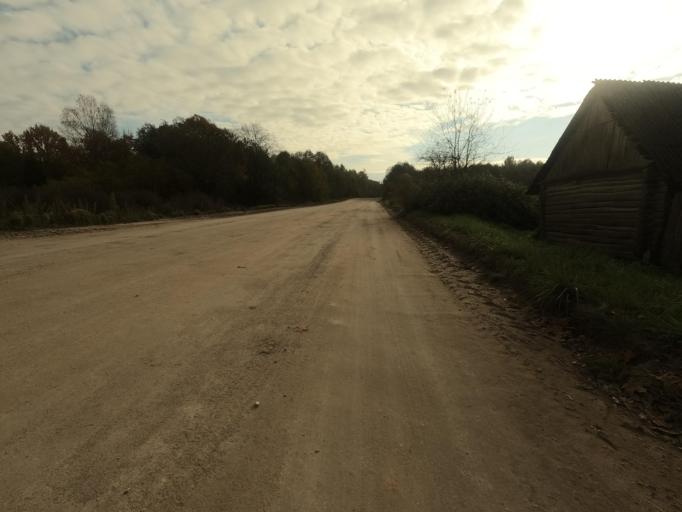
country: RU
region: Novgorod
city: Batetskiy
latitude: 58.8007
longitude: 30.6289
